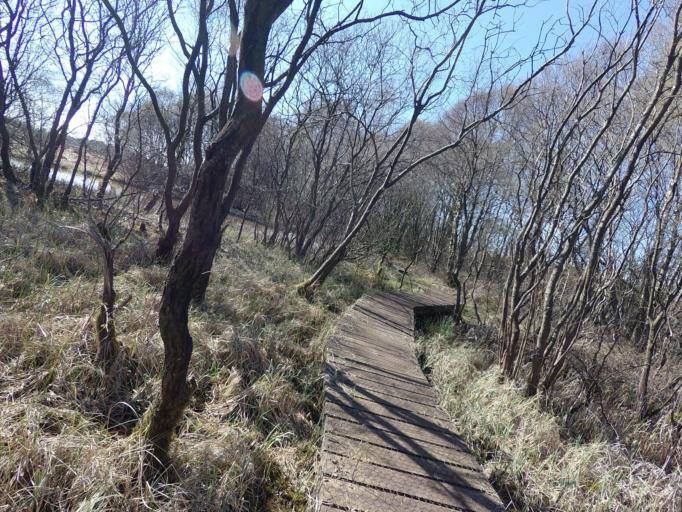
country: GB
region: Scotland
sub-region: West Lothian
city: West Calder
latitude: 55.8944
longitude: -3.5853
